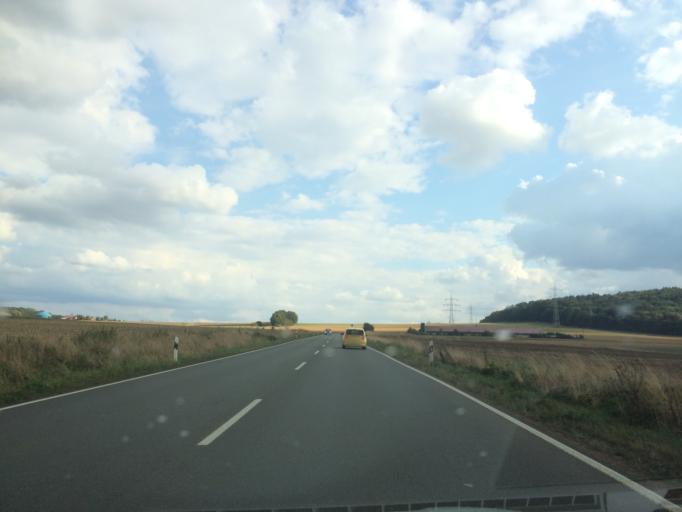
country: DE
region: Hesse
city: Trendelburg
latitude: 51.5348
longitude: 9.4103
